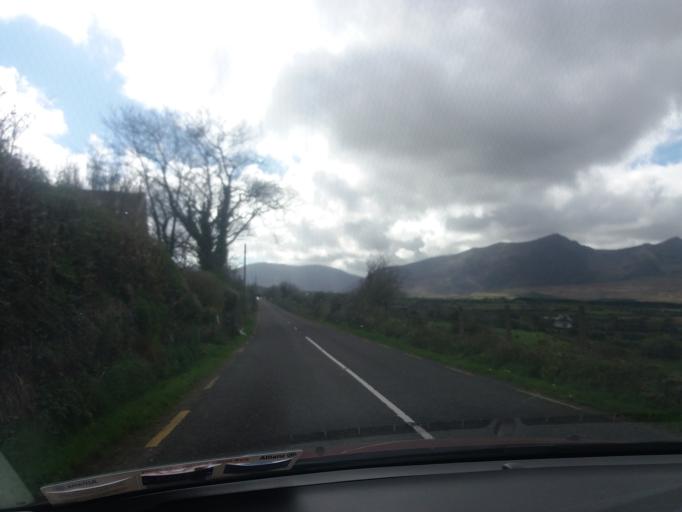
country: IE
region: Munster
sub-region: Ciarrai
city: Dingle
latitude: 52.2250
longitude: -10.1359
